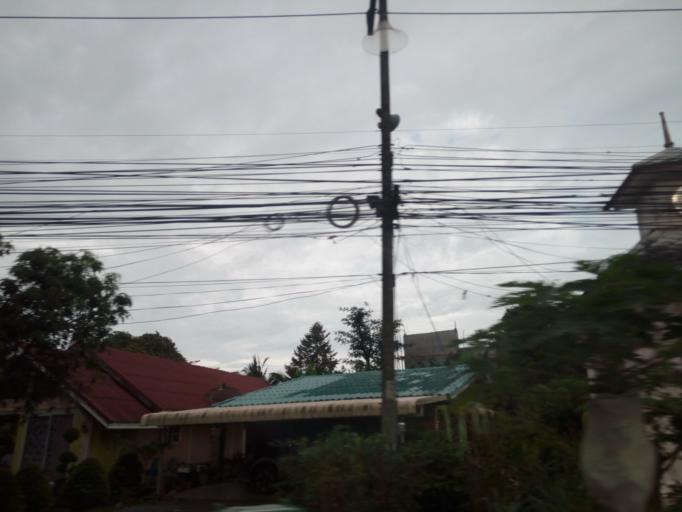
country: TH
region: Phuket
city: Thalang
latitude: 8.0525
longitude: 98.4103
